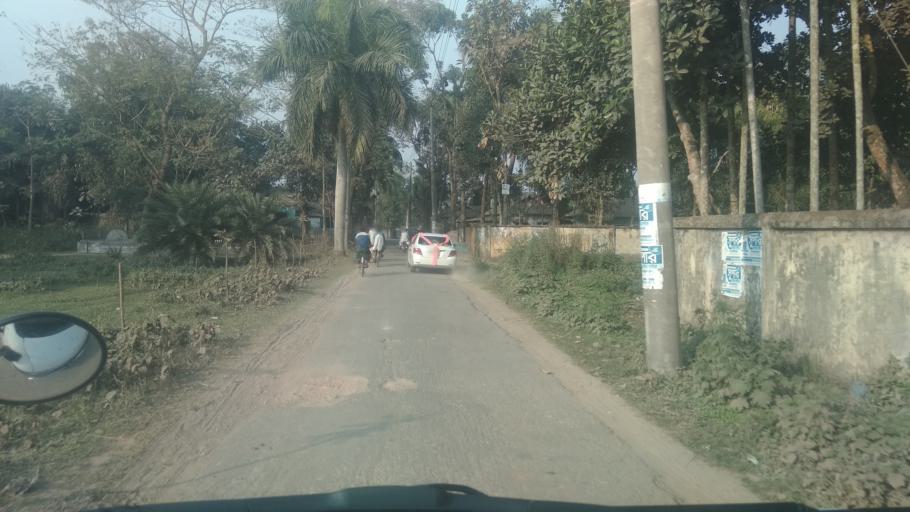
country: BD
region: Dhaka
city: Mymensingh
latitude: 24.7571
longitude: 90.5661
